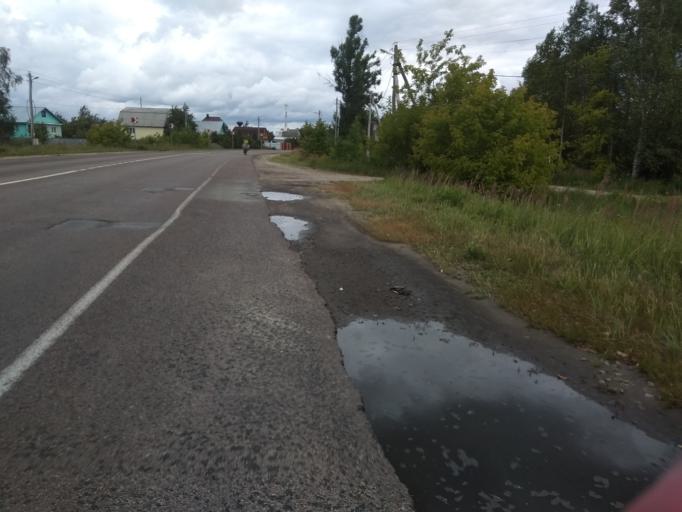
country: RU
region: Moskovskaya
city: Kerva
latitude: 55.5917
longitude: 39.7008
